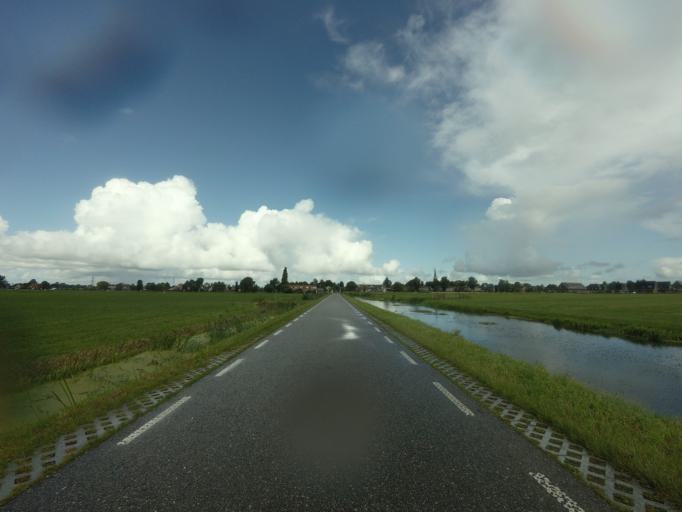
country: NL
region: Friesland
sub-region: Gemeente Leeuwarden
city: Wirdum
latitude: 53.1448
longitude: 5.8032
